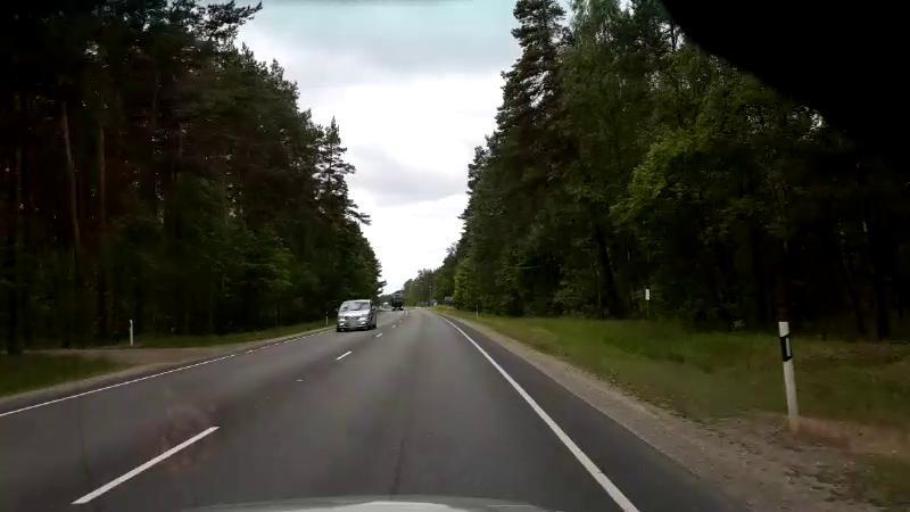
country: EE
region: Paernumaa
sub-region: Paikuse vald
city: Paikuse
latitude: 58.2830
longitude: 24.5751
